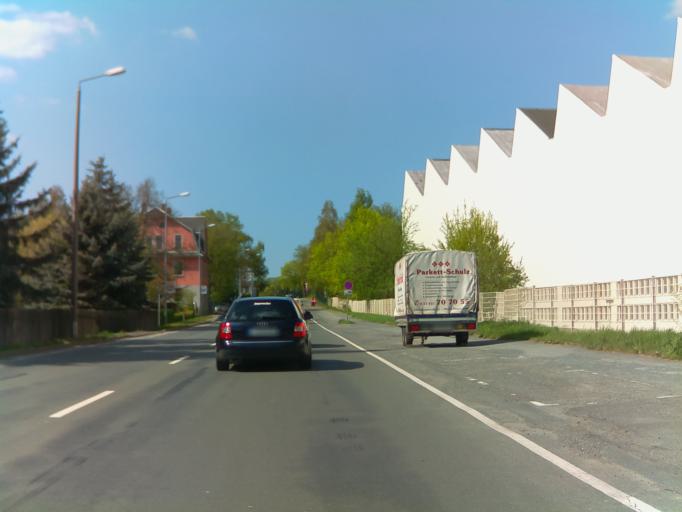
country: DE
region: Saxony
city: Syrau
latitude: 50.5271
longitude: 12.1099
